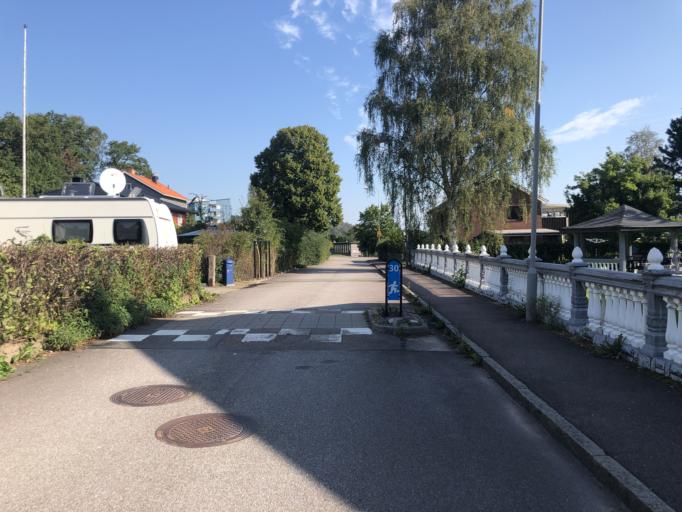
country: SE
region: Vaestra Goetaland
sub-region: Goteborg
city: Goeteborg
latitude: 57.7502
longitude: 11.9790
